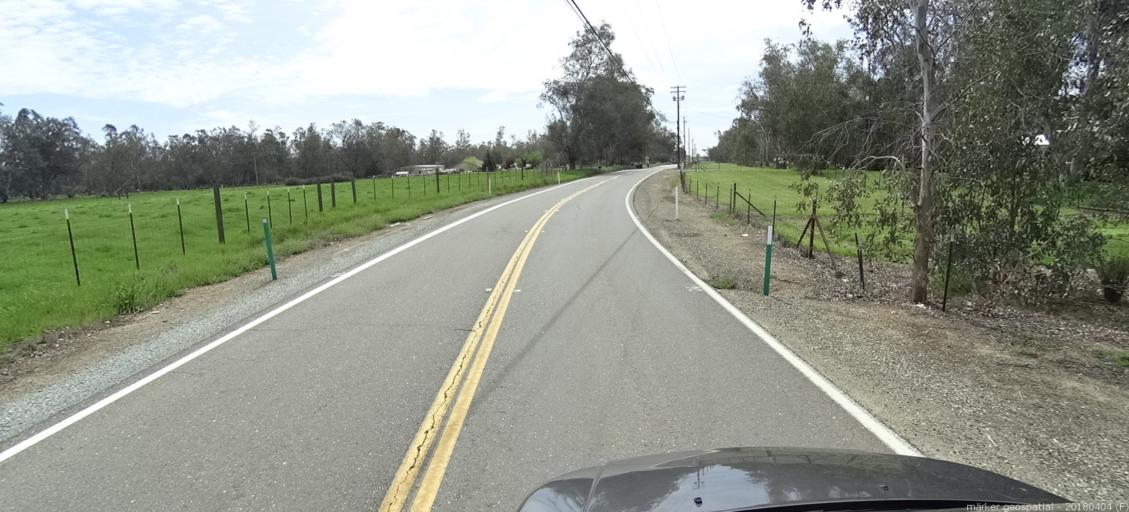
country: US
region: California
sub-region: Sacramento County
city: Clay
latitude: 38.2994
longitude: -121.1720
